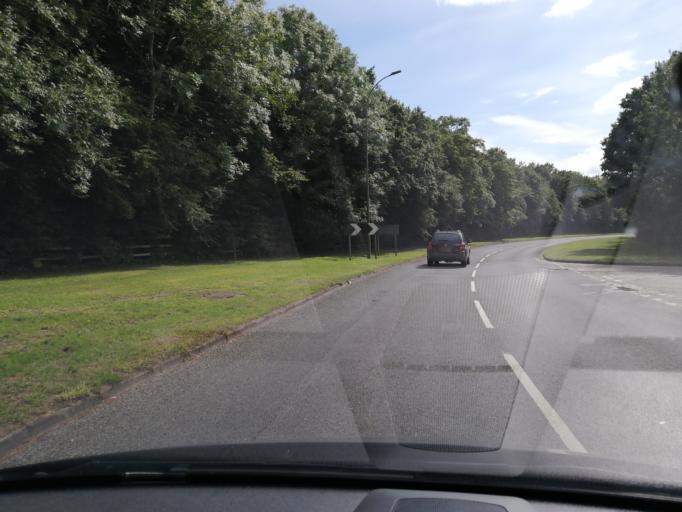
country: GB
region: England
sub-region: Cambridgeshire
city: Yaxley
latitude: 52.5389
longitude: -0.2947
